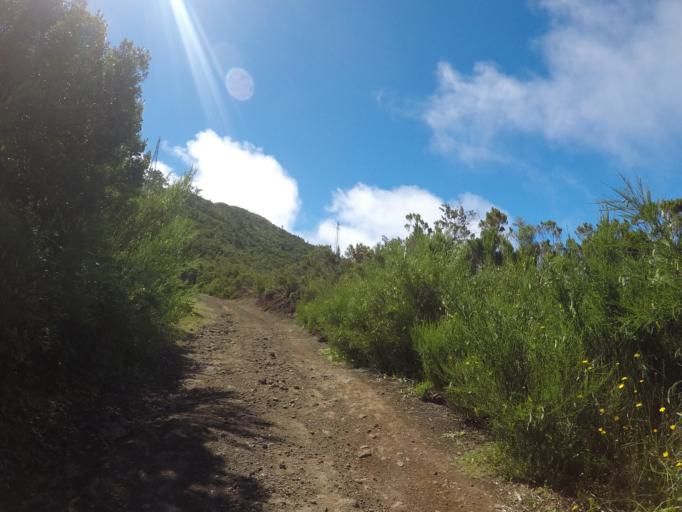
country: PT
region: Madeira
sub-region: Sao Vicente
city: Sao Vicente
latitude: 32.7733
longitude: -17.0626
